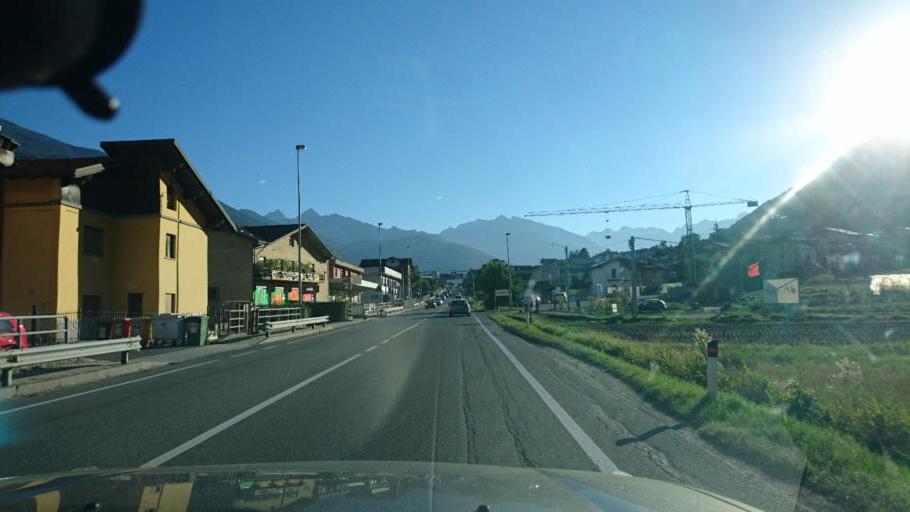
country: IT
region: Aosta Valley
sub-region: Valle d'Aosta
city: Montan-Angelin-Arensod
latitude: 45.7283
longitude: 7.2814
